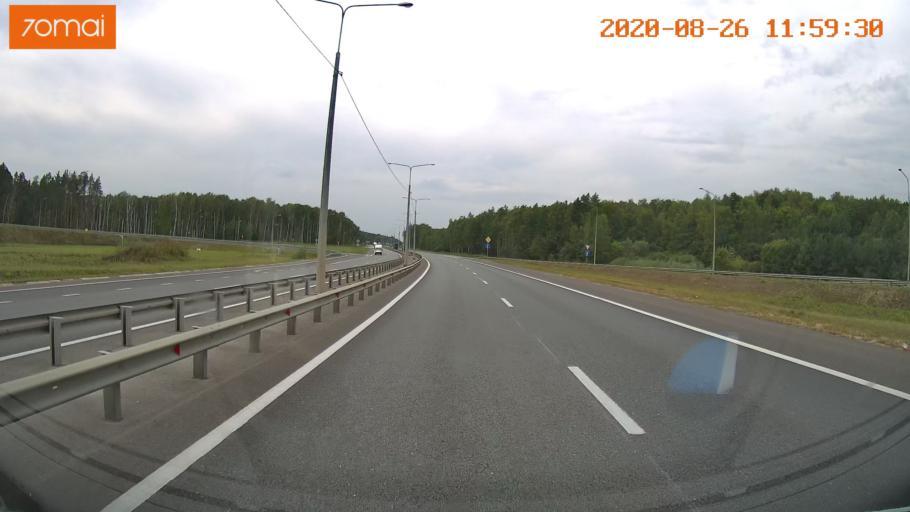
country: RU
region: Rjazan
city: Kiritsy
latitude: 54.2860
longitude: 40.2982
